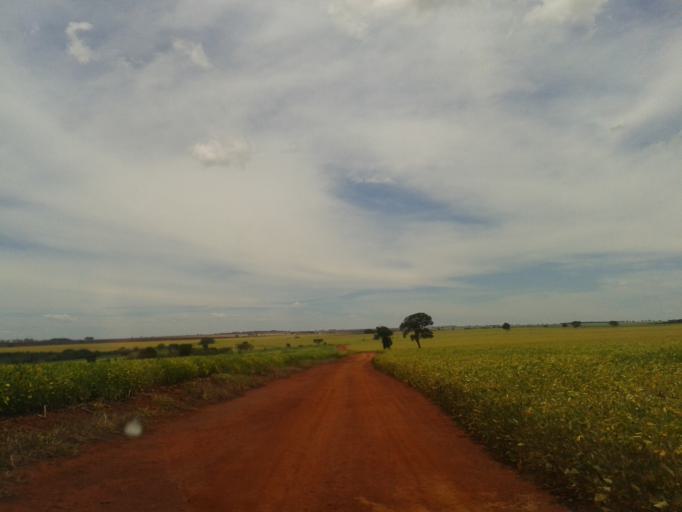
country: BR
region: Minas Gerais
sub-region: Capinopolis
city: Capinopolis
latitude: -18.6711
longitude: -49.7252
